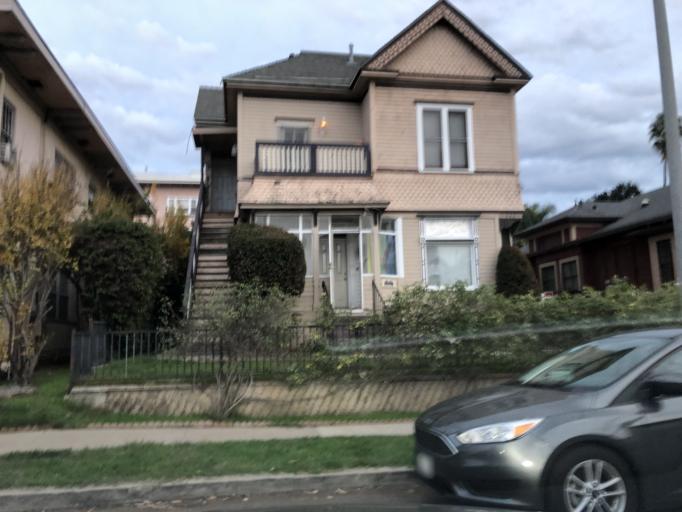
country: US
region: California
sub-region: San Diego County
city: San Diego
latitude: 32.7154
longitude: -117.1458
